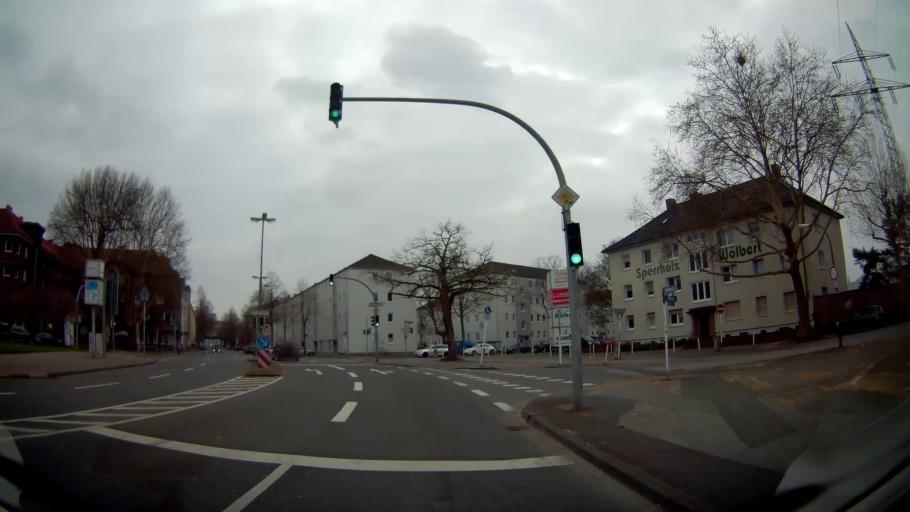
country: DE
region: North Rhine-Westphalia
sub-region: Regierungsbezirk Arnsberg
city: Dortmund
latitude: 51.5186
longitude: 7.4877
